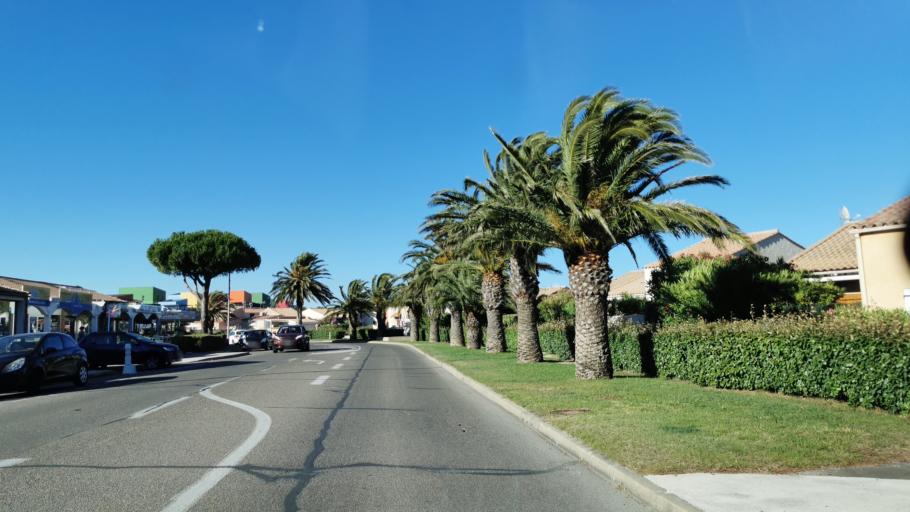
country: FR
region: Languedoc-Roussillon
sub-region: Departement de l'Aude
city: Gruissan
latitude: 43.1119
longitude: 3.1031
